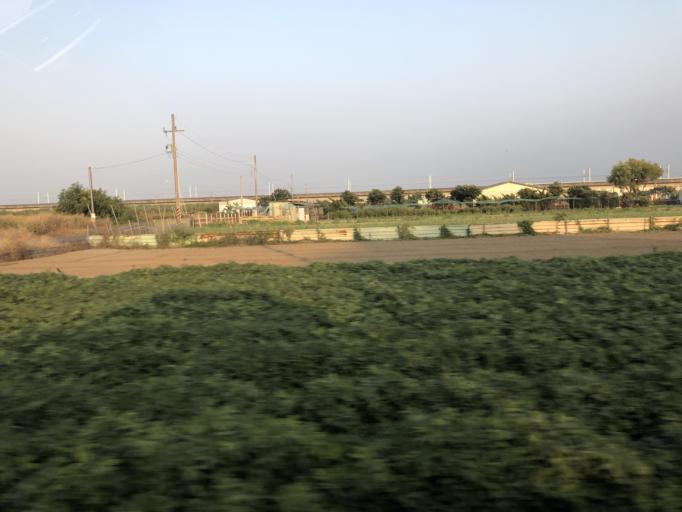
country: TW
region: Taiwan
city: Xinying
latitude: 23.1487
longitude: 120.2732
